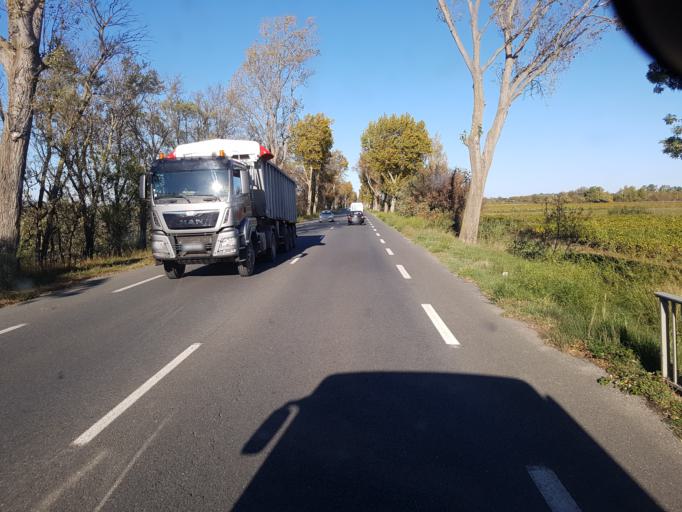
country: FR
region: Languedoc-Roussillon
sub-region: Departement de l'Aude
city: Coursan
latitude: 43.2147
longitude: 3.0334
